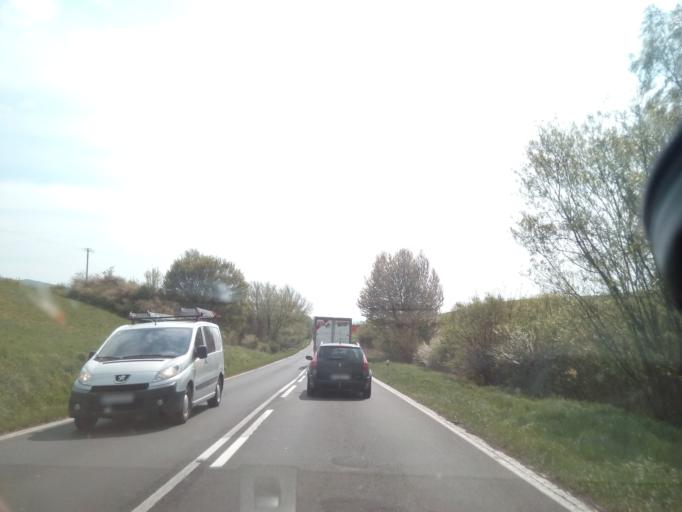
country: SK
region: Presovsky
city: Giraltovce
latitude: 49.0400
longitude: 21.4510
